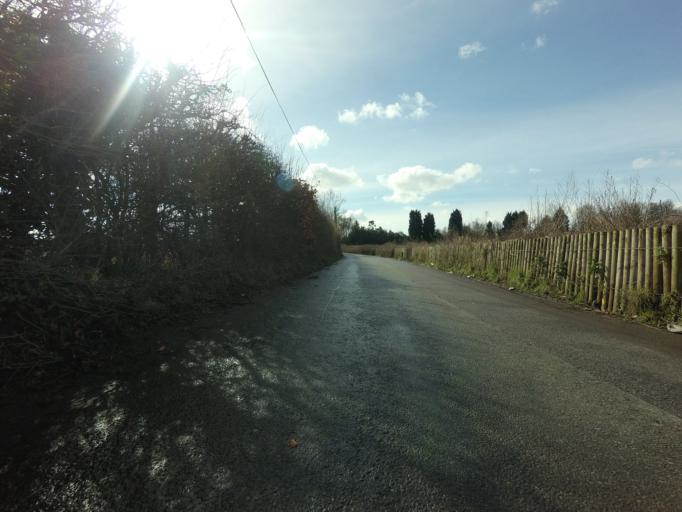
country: GB
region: England
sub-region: Greater London
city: Orpington
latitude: 51.3893
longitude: 0.1342
